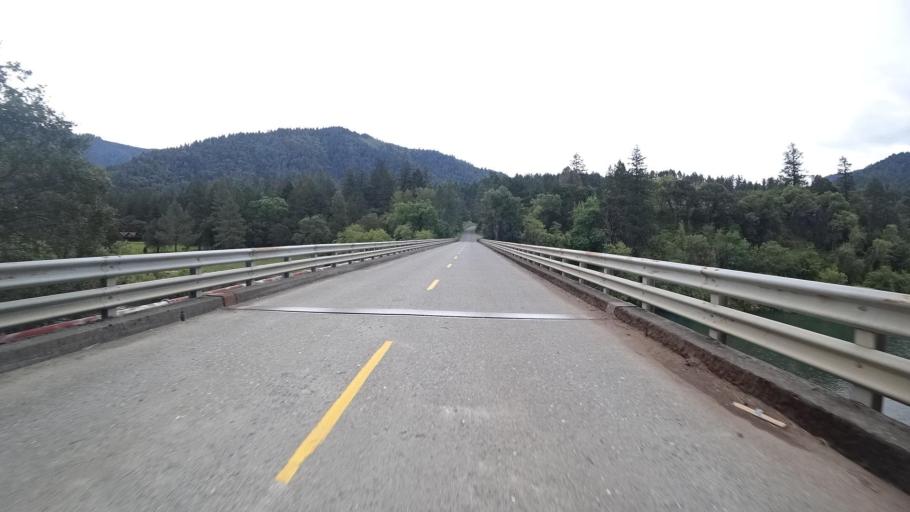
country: US
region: California
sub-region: Humboldt County
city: Willow Creek
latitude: 40.9463
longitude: -123.6247
